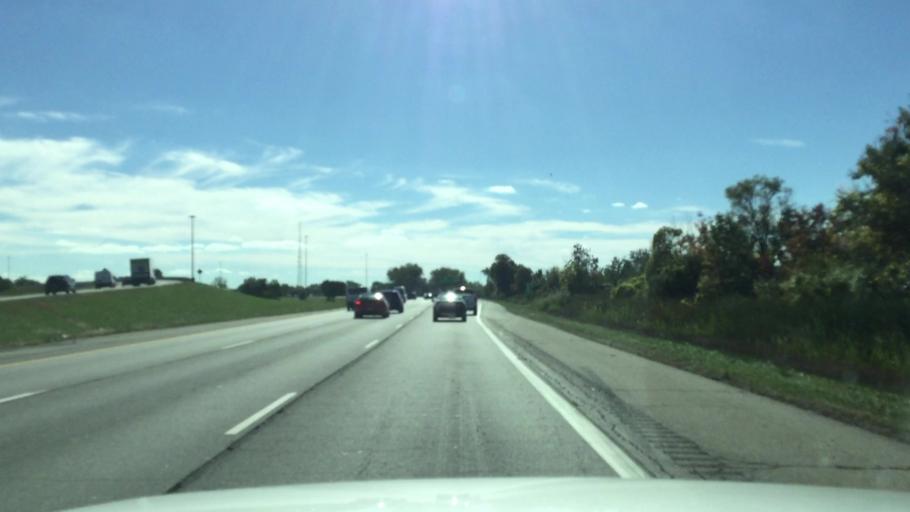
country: US
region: Michigan
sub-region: Wayne County
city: Plymouth
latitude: 42.3948
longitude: -83.4333
